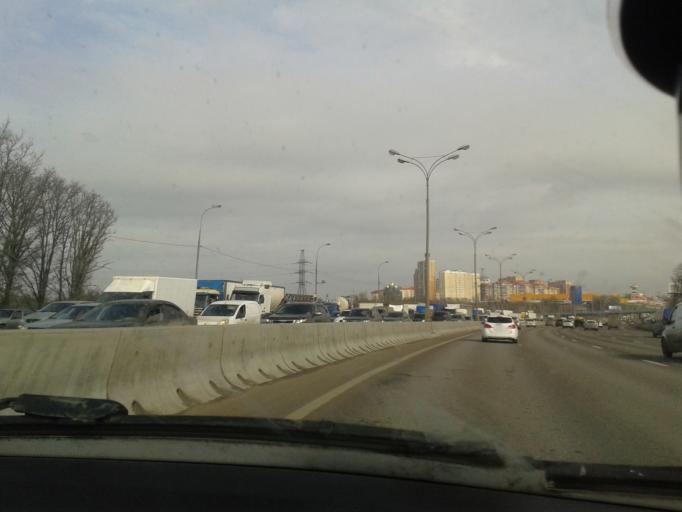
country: RU
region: Moscow
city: Strogino
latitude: 55.8468
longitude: 37.3919
